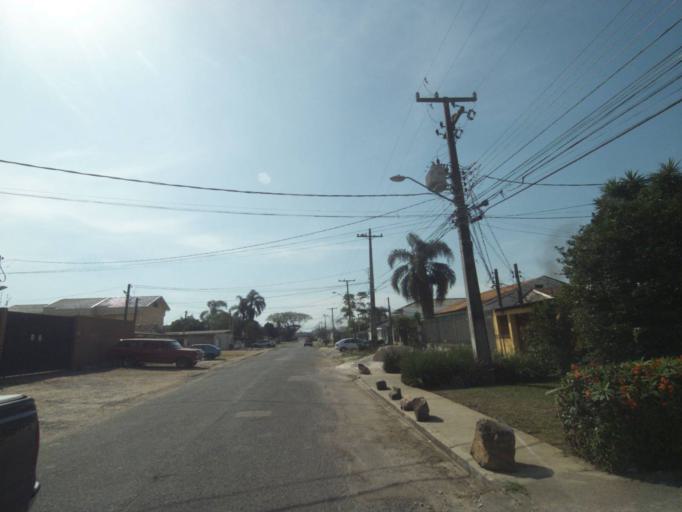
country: BR
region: Parana
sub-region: Sao Jose Dos Pinhais
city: Sao Jose dos Pinhais
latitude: -25.4878
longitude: -49.2345
